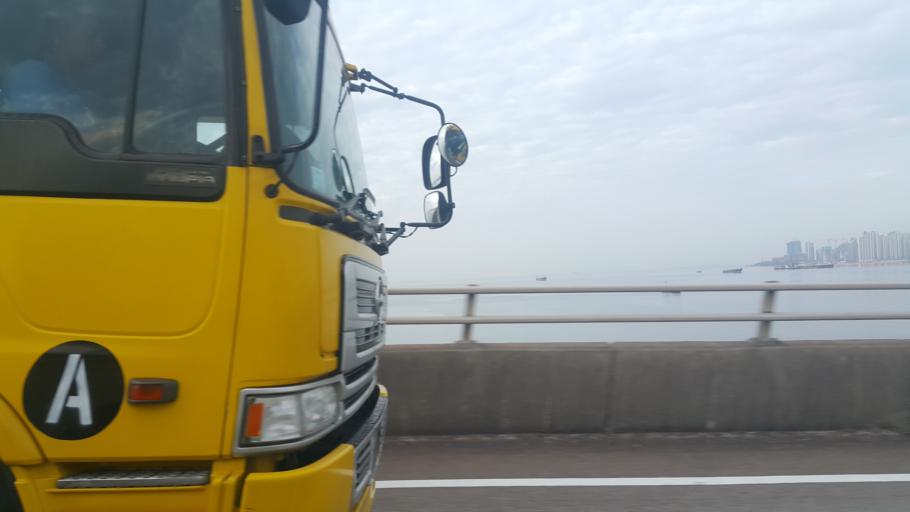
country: MY
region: Johor
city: Johor Bahru
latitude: 1.3545
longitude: 103.6281
